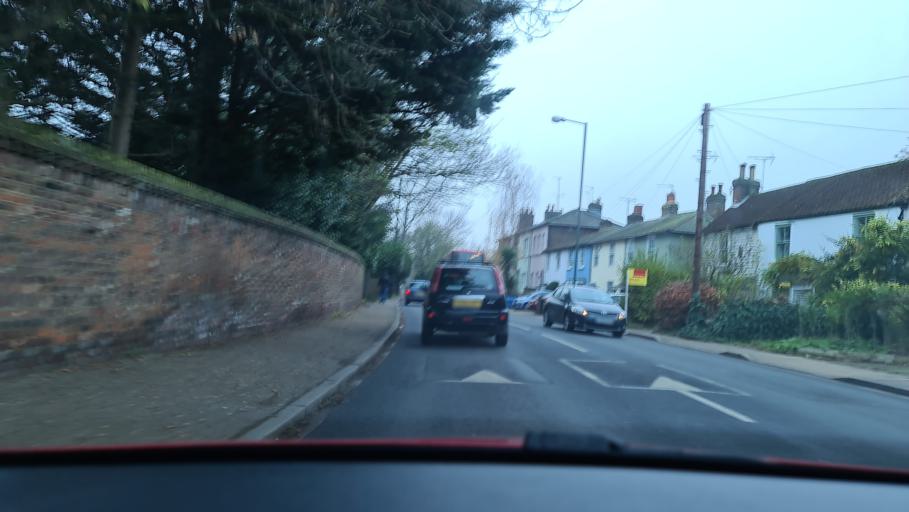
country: GB
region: England
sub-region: Greater London
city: Richmond
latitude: 51.4420
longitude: -0.3033
